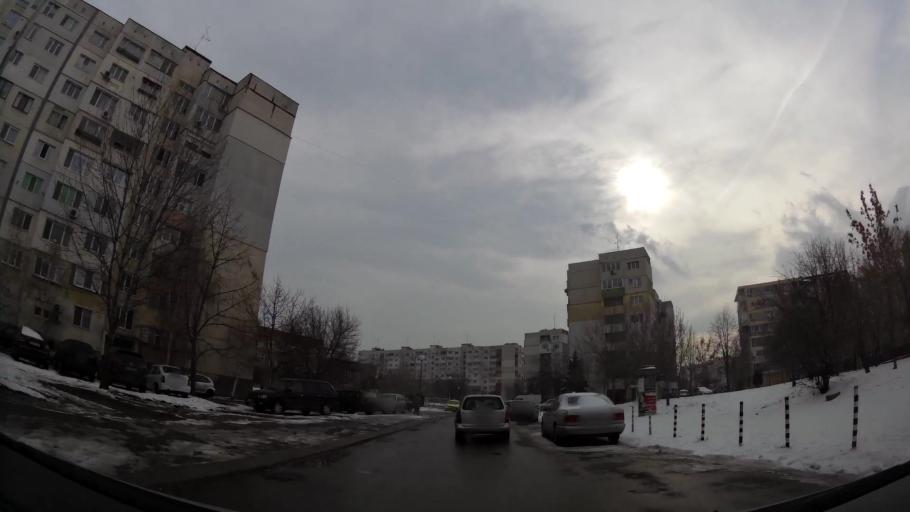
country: BG
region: Sofia-Capital
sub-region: Stolichna Obshtina
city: Sofia
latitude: 42.7141
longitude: 23.3768
